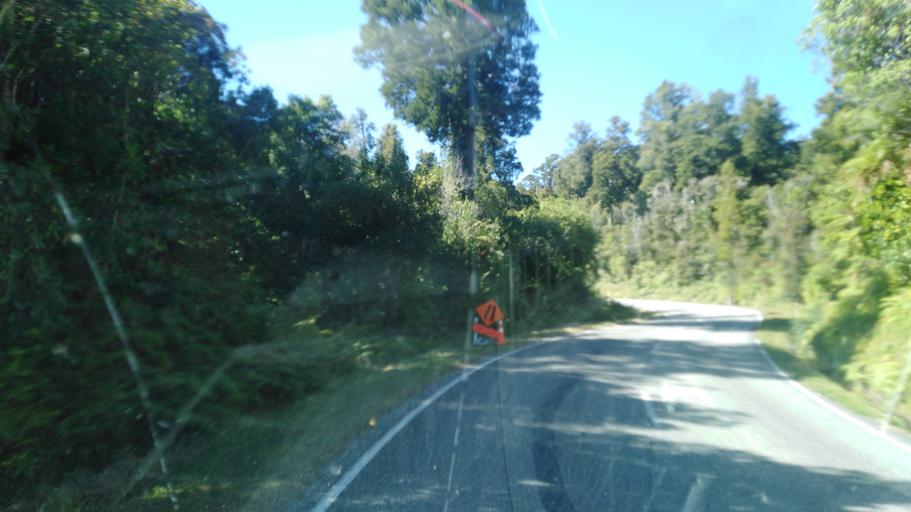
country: NZ
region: West Coast
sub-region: Buller District
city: Westport
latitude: -41.5270
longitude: 172.0031
